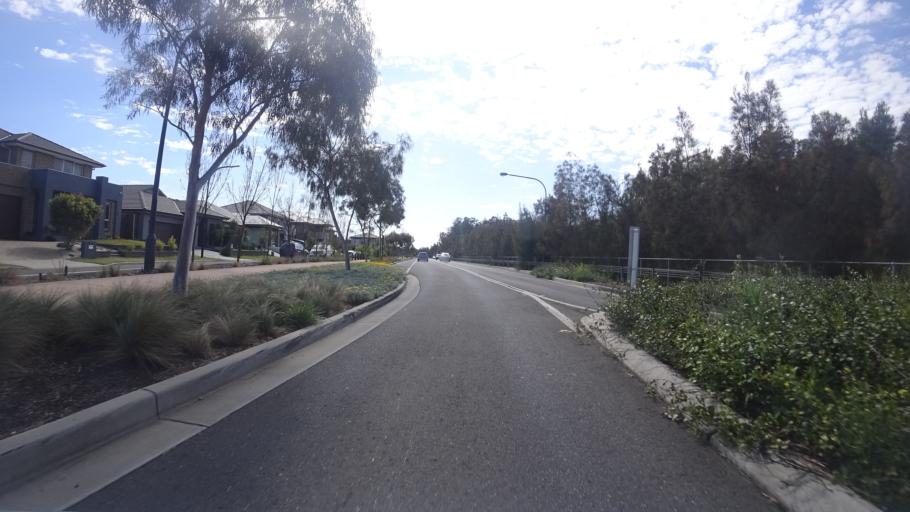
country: AU
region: New South Wales
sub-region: Bankstown
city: Milperra
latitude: -33.9367
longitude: 150.9602
